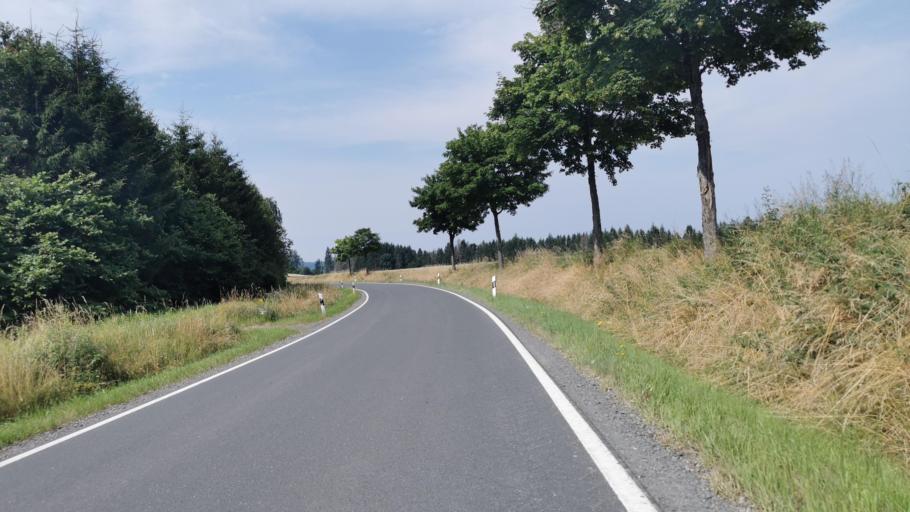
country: DE
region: Bavaria
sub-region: Upper Franconia
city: Wilhelmsthal
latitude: 50.3199
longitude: 11.4149
